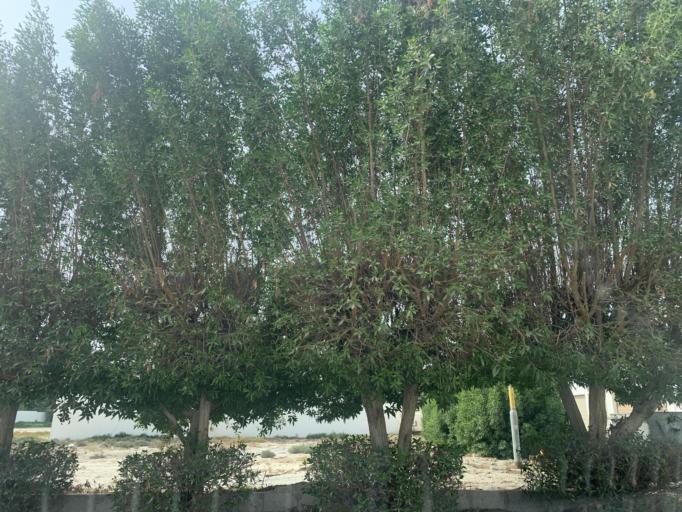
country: BH
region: Manama
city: Jidd Hafs
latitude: 26.2019
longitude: 50.4783
